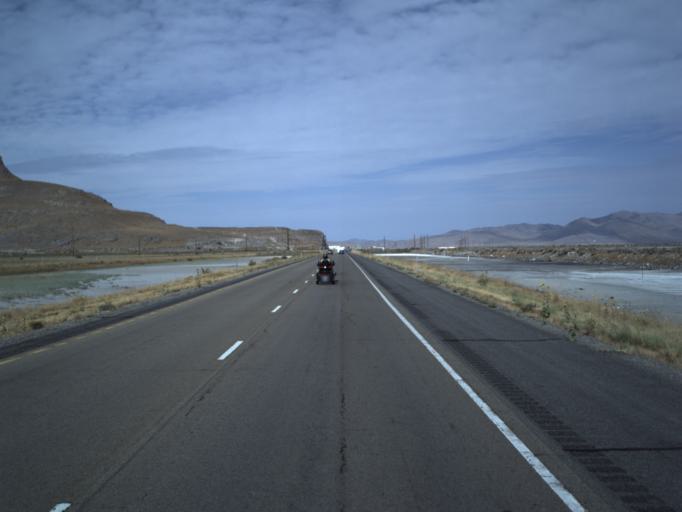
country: US
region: Utah
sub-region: Tooele County
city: Grantsville
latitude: 40.7387
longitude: -112.6171
